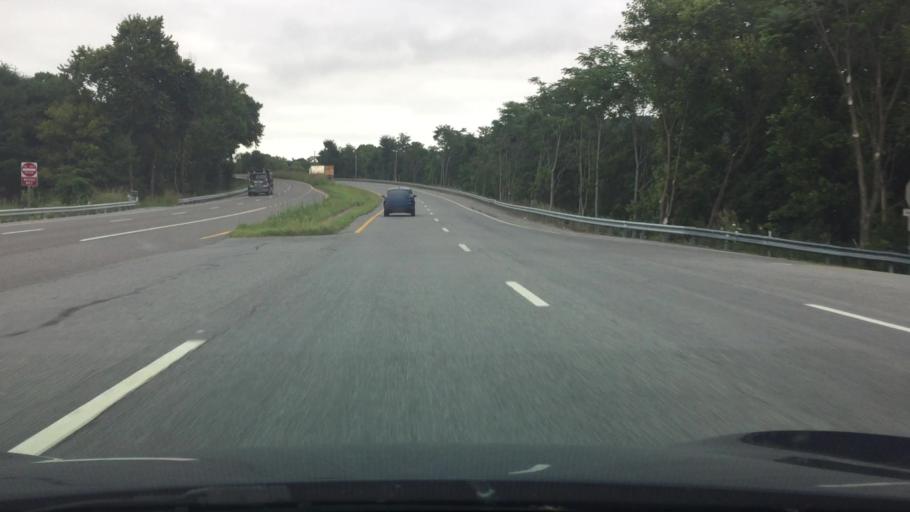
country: US
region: Virginia
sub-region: Montgomery County
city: Shawsville
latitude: 37.2214
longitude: -80.2228
